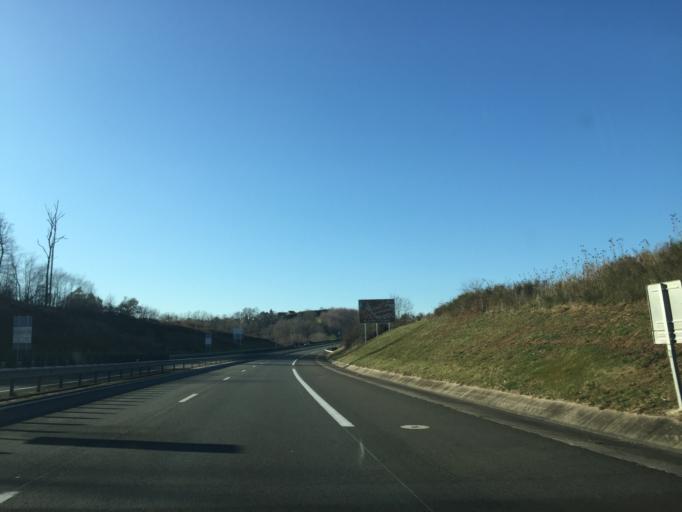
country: FR
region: Limousin
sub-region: Departement de la Correze
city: Saint-Pantaleon-de-Larche
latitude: 45.1614
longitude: 1.4325
